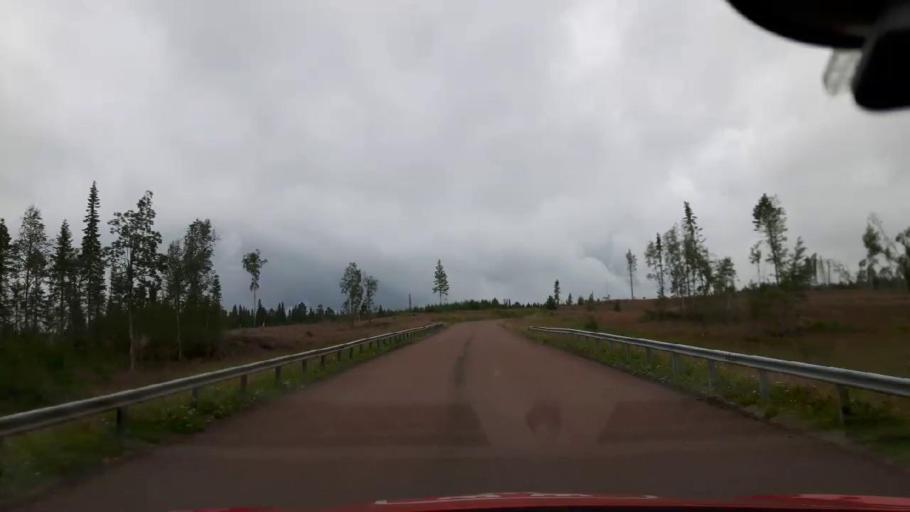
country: SE
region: Jaemtland
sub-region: Krokoms Kommun
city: Valla
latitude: 63.3742
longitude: 13.7568
